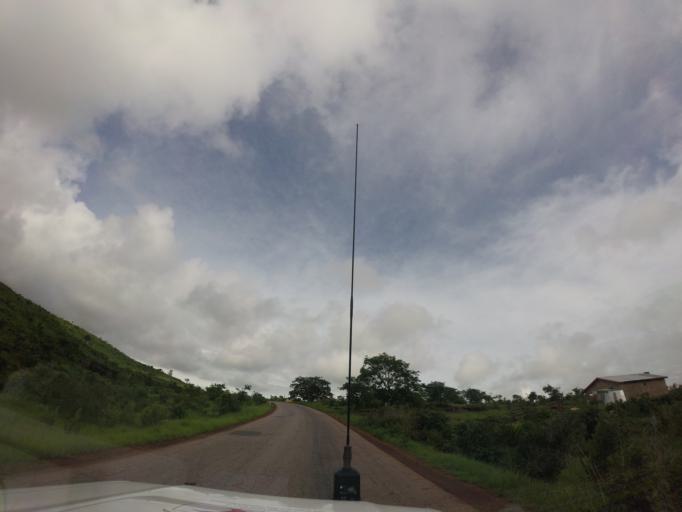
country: GN
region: Kindia
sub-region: Coyah
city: Coyah
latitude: 9.8347
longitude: -13.2292
